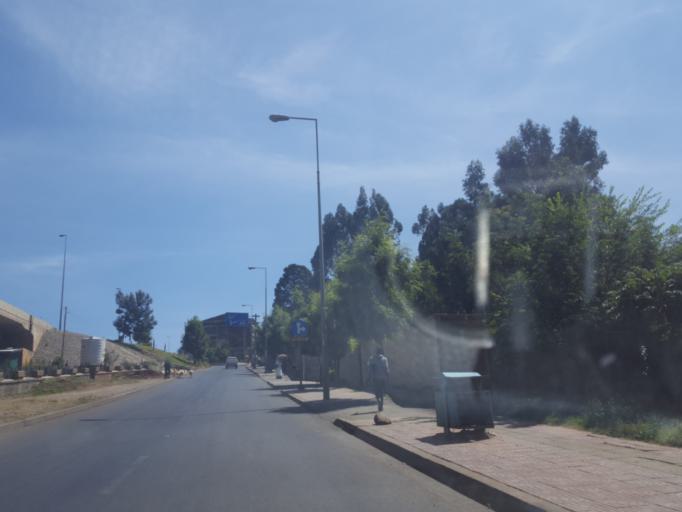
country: ET
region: Adis Abeba
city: Addis Ababa
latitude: 9.0644
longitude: 38.7286
